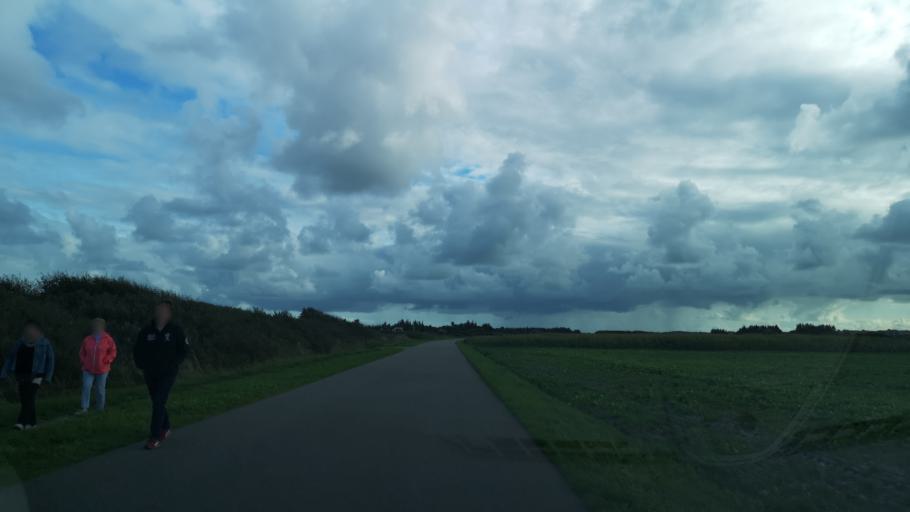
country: DK
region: Central Jutland
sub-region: Ringkobing-Skjern Kommune
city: Ringkobing
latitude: 56.1369
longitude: 8.1333
